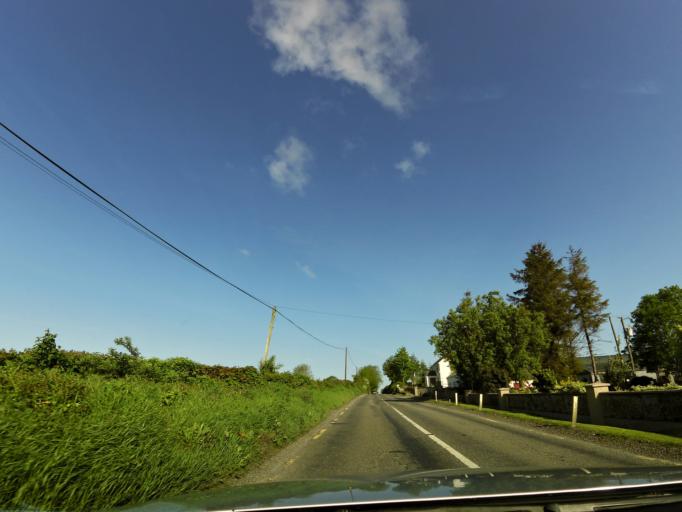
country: IE
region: Munster
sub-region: North Tipperary
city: Nenagh
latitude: 52.8435
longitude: -8.1442
